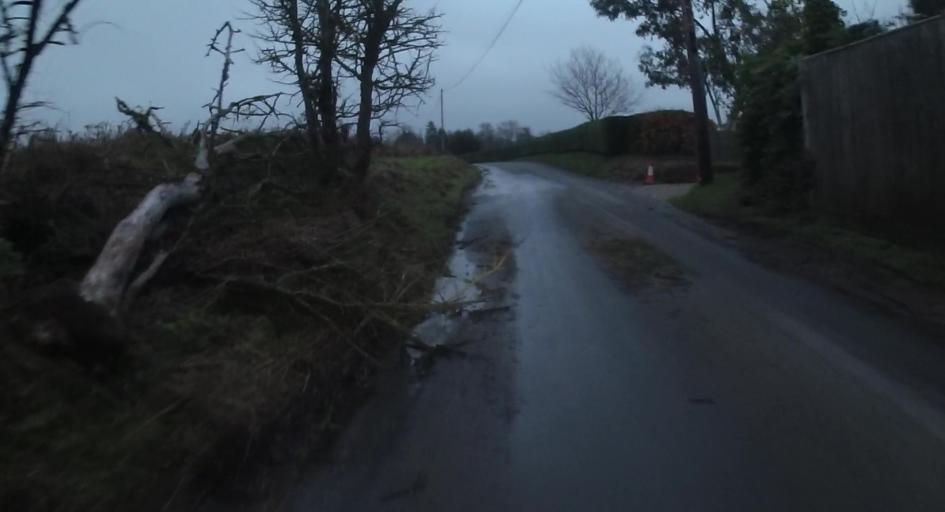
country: GB
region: England
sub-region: Hampshire
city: Tadley
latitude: 51.3423
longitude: -1.0871
